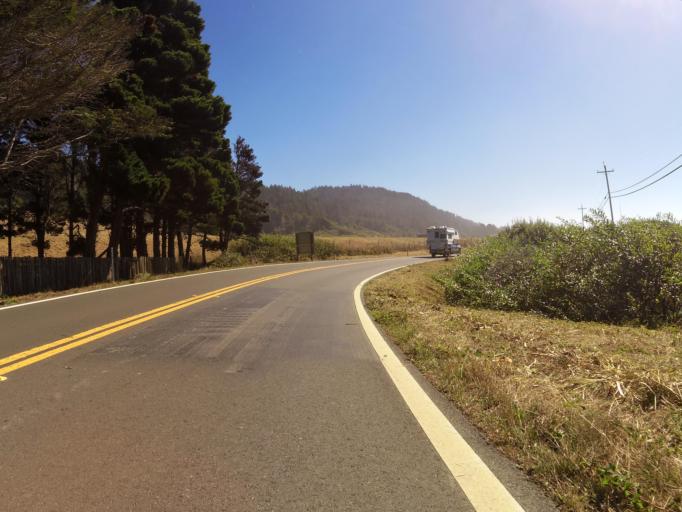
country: US
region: California
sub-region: Mendocino County
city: Fort Bragg
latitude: 39.6444
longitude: -123.7841
